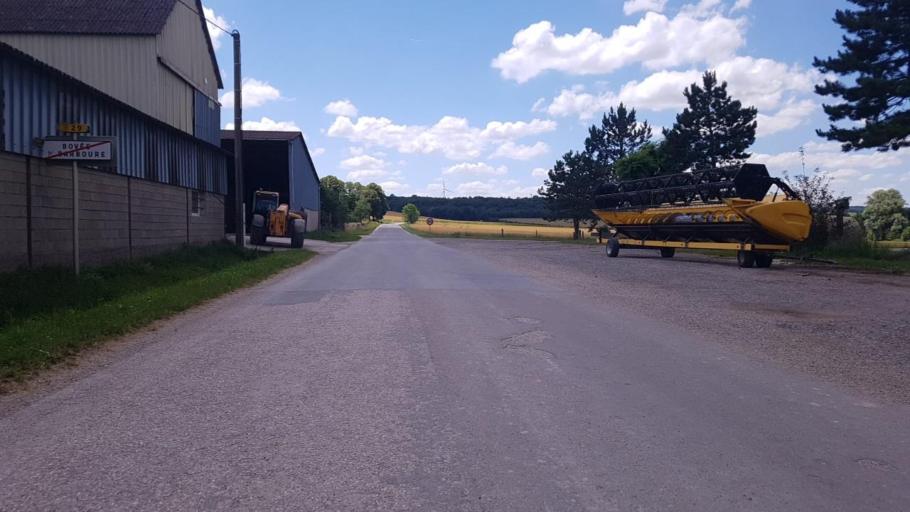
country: FR
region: Lorraine
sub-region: Departement de la Meuse
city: Vacon
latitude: 48.6423
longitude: 5.5104
